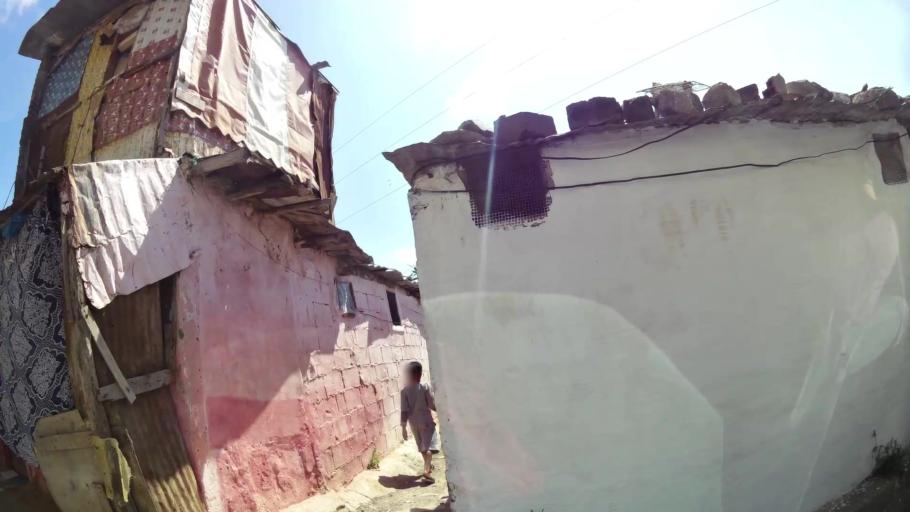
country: MA
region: Rabat-Sale-Zemmour-Zaer
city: Sale
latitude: 34.0360
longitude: -6.7991
